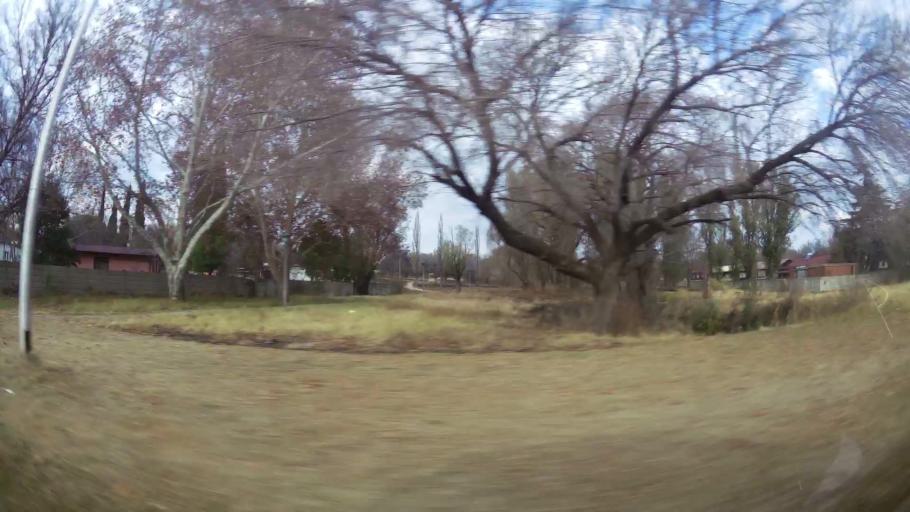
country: ZA
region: Orange Free State
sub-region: Fezile Dabi District Municipality
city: Sasolburg
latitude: -26.8093
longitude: 27.8104
